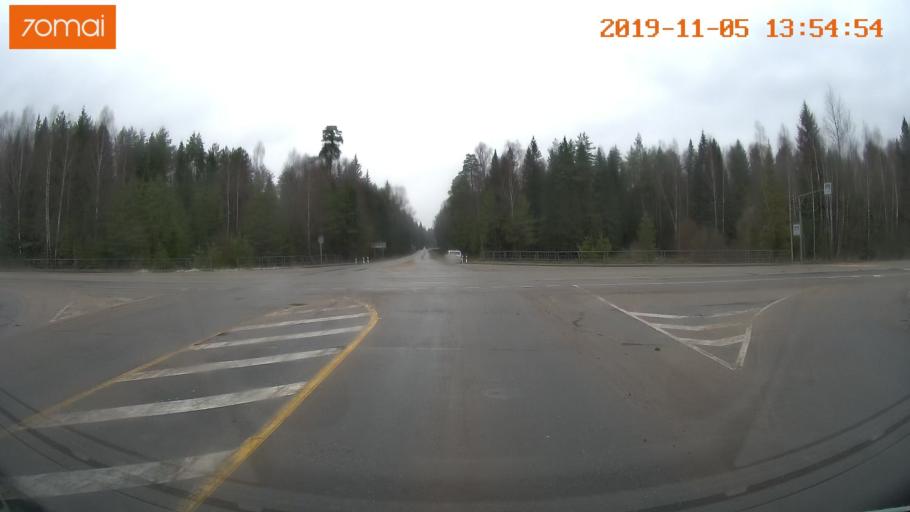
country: RU
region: Ivanovo
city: Kaminskiy
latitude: 57.0484
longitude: 41.3629
